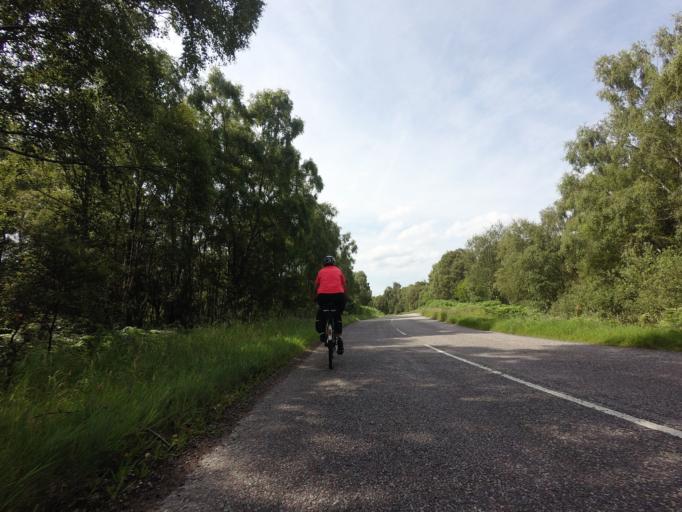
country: GB
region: Scotland
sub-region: Highland
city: Alness
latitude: 57.8580
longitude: -4.2370
